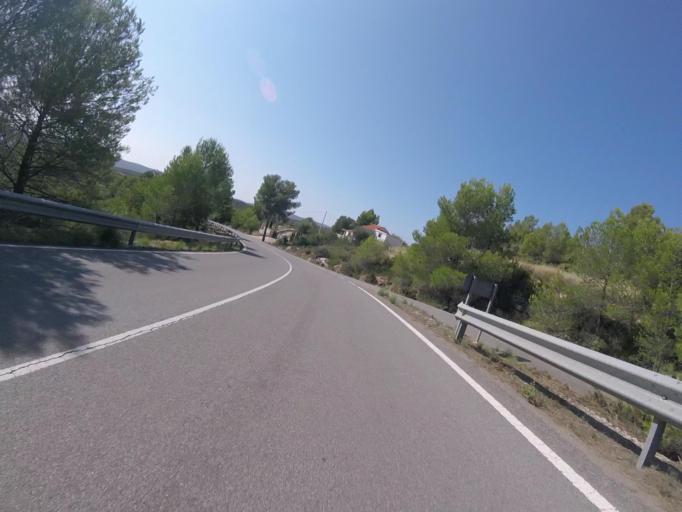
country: ES
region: Valencia
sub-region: Provincia de Castello
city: Adzaneta
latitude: 40.2381
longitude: -0.1892
